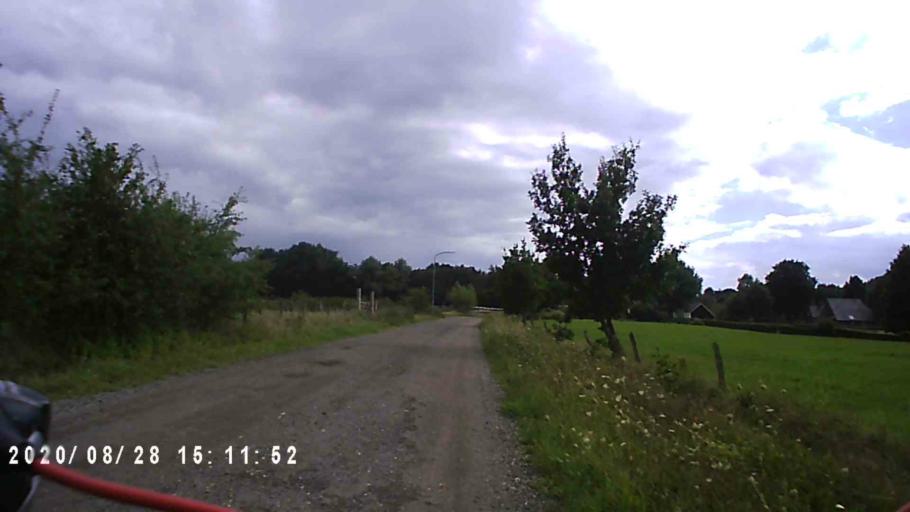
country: NL
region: Drenthe
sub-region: Gemeente Tynaarlo
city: Vries
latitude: 53.1275
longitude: 6.5741
